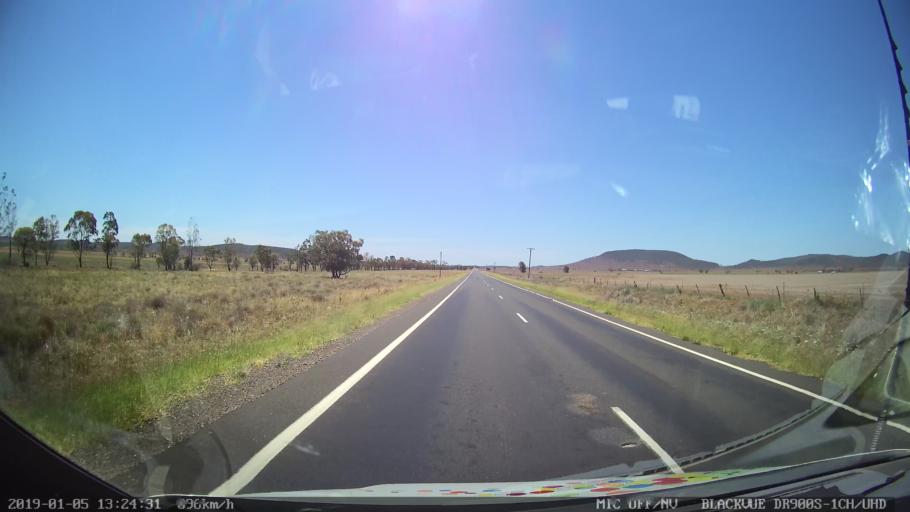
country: AU
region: New South Wales
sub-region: Gunnedah
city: Gunnedah
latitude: -31.0688
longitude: 149.9901
